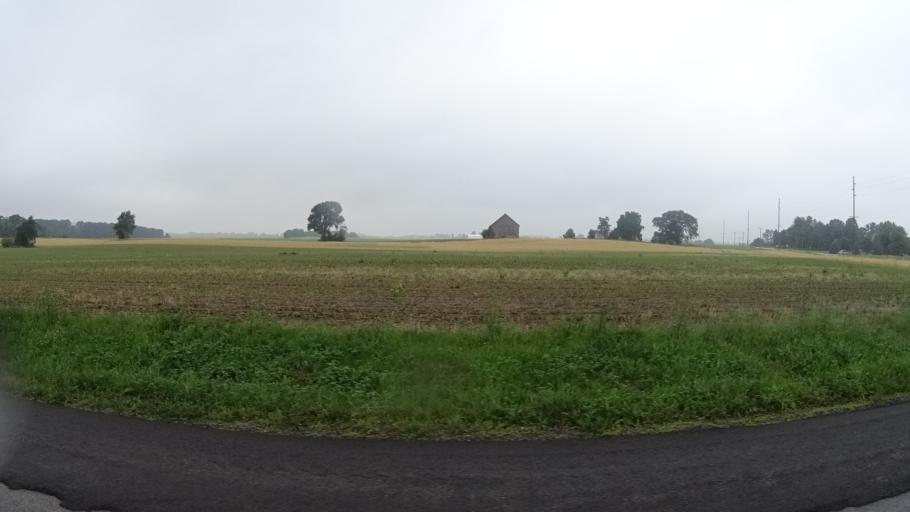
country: US
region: Ohio
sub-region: Huron County
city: Bellevue
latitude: 41.2988
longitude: -82.8325
